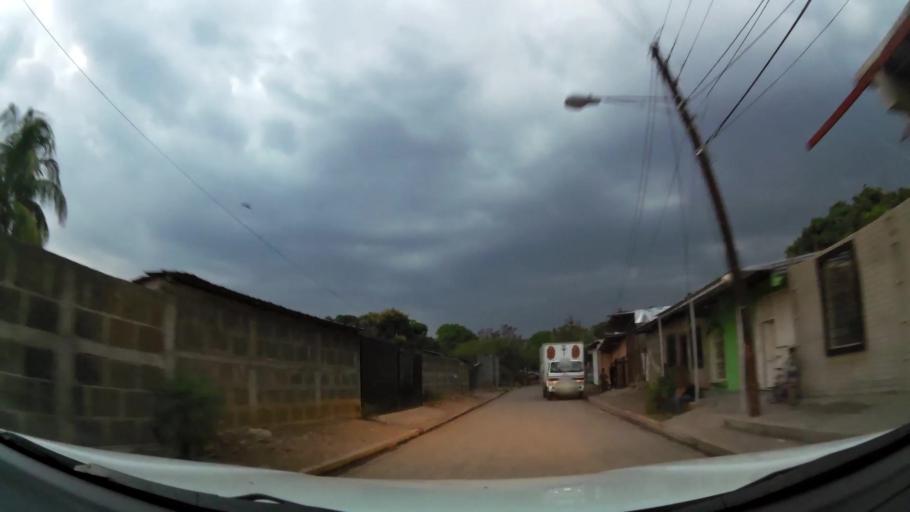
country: NI
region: Matagalpa
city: Ciudad Dario
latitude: 12.8571
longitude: -86.0958
